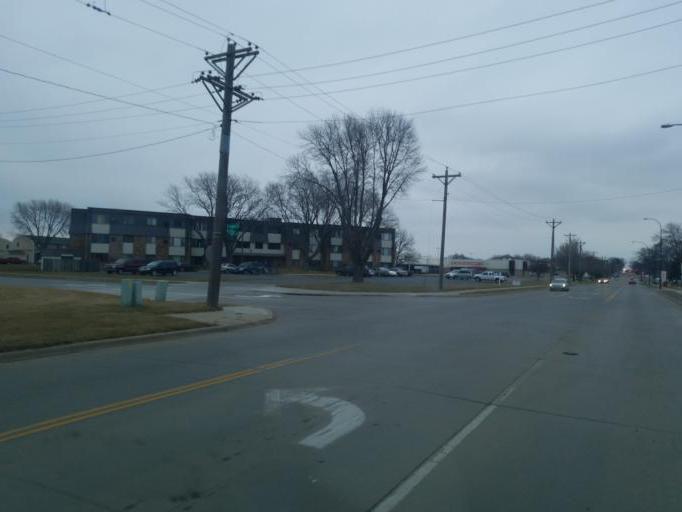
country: US
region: South Dakota
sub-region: Yankton County
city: Yankton
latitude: 42.8906
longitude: -97.4027
